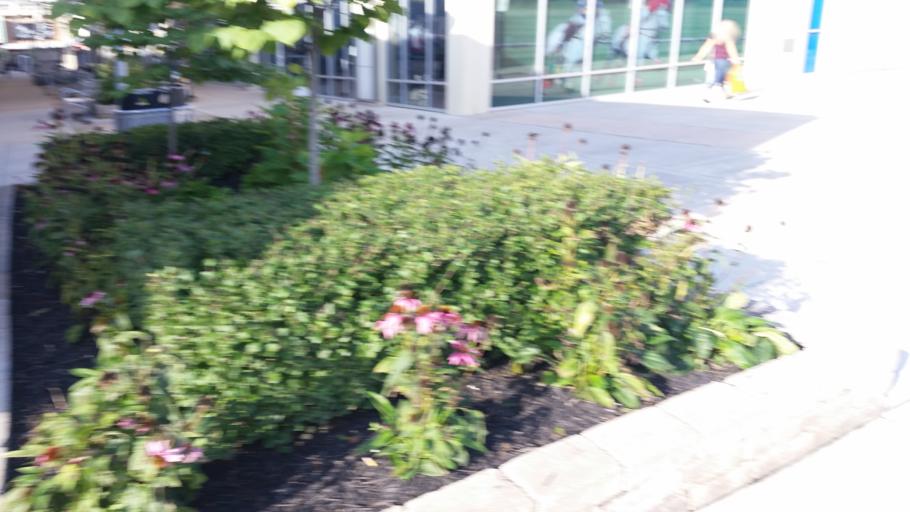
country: CA
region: Ontario
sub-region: Halton
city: Milton
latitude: 43.5755
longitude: -79.8299
